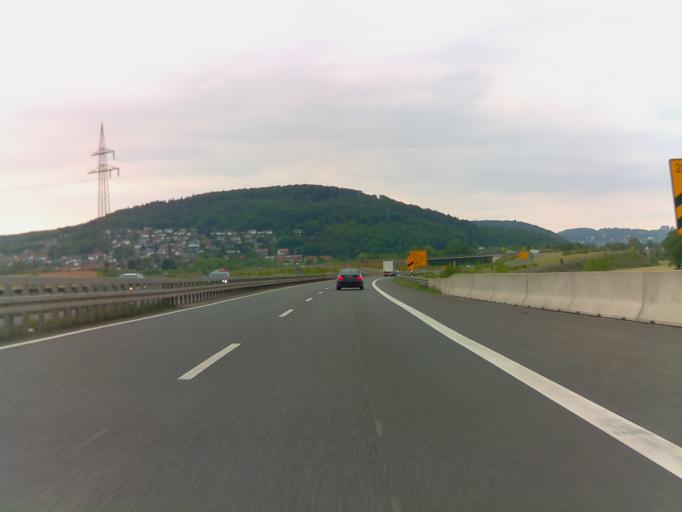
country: DE
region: Hesse
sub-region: Regierungsbezirk Giessen
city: Fronhausen
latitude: 50.7478
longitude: 8.7402
